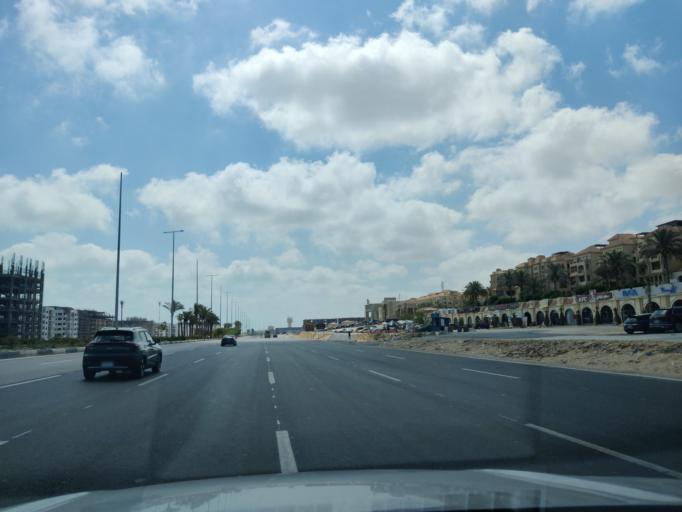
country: EG
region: Muhafazat Matruh
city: Al `Alamayn
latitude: 30.8459
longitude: 28.9319
